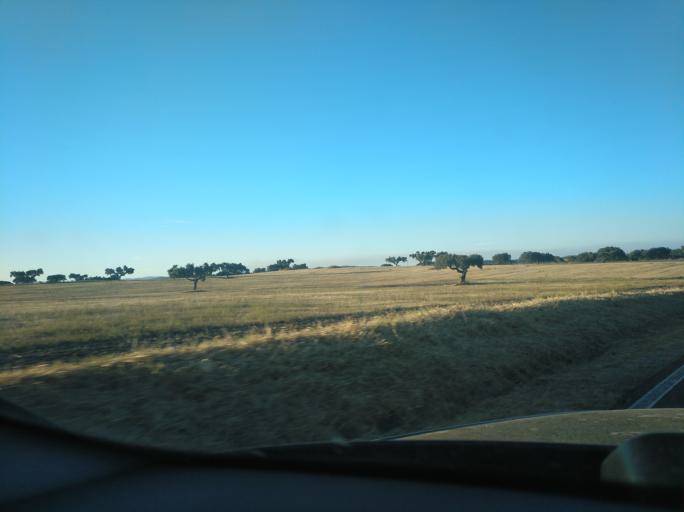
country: PT
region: Portalegre
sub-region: Arronches
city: Arronches
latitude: 39.0743
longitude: -7.1769
